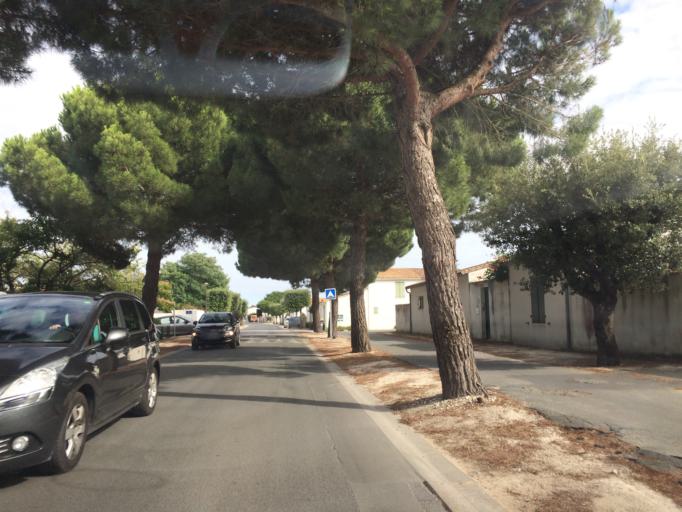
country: FR
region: Poitou-Charentes
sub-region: Departement de la Charente-Maritime
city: La Flotte
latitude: 46.1861
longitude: -1.3329
